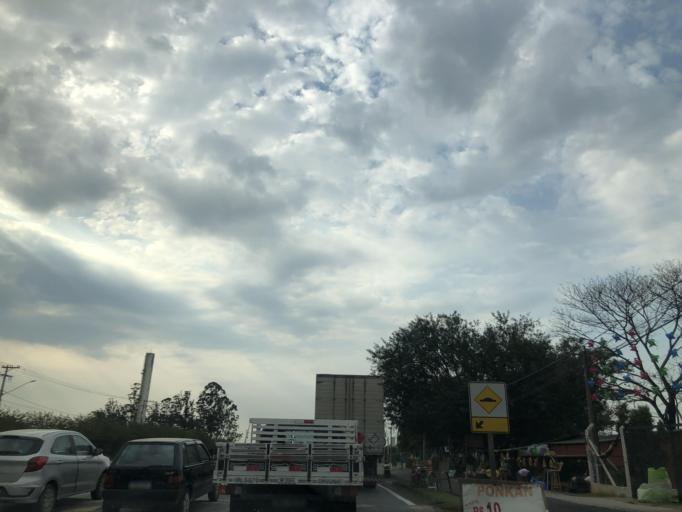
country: BR
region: Sao Paulo
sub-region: Sorocaba
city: Sorocaba
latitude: -23.5382
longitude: -47.4875
